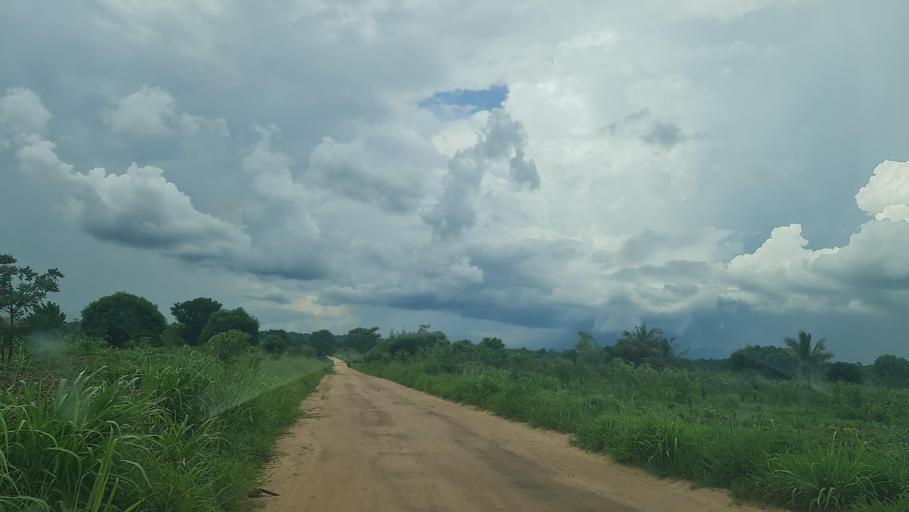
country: MW
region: Southern Region
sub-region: Nsanje District
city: Nsanje
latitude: -17.5800
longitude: 35.6621
